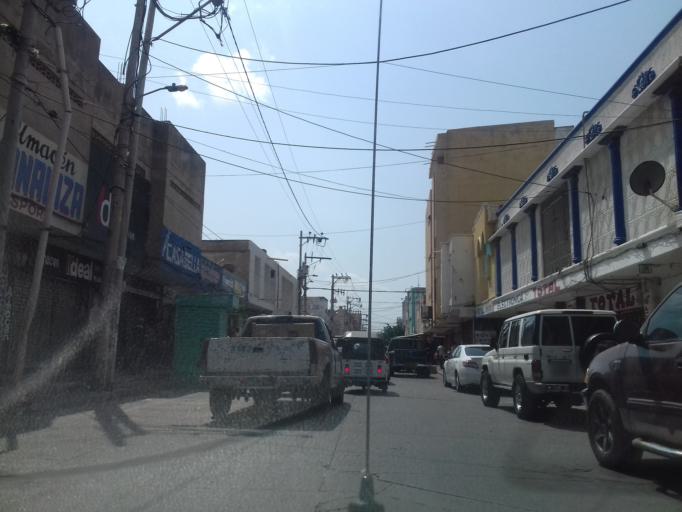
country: CO
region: La Guajira
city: Maicao
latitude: 11.3785
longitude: -72.2380
